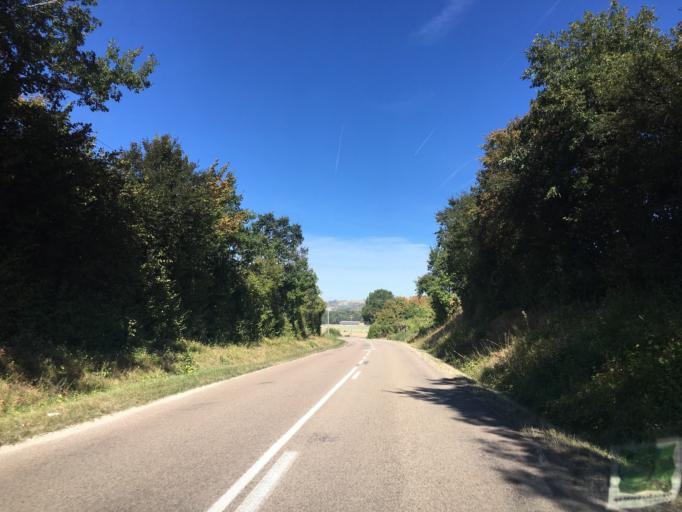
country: FR
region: Bourgogne
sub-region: Departement de l'Yonne
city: Saint-Bris-le-Vineux
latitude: 47.6850
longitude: 3.6533
